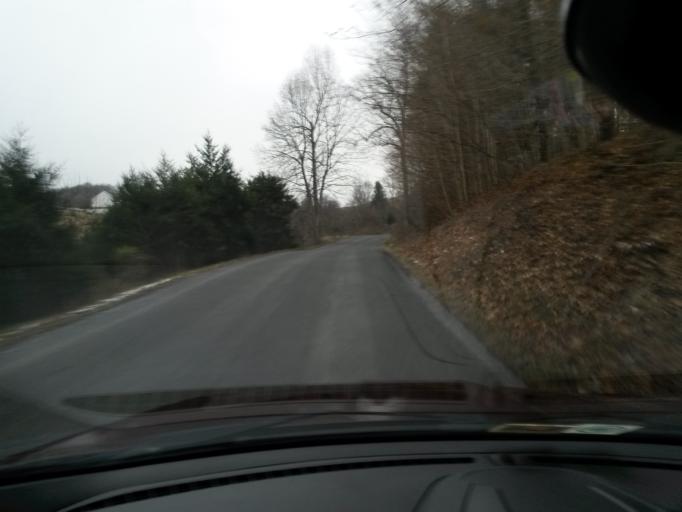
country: US
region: Virginia
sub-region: Rockbridge County
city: East Lexington
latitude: 37.9406
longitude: -79.2558
